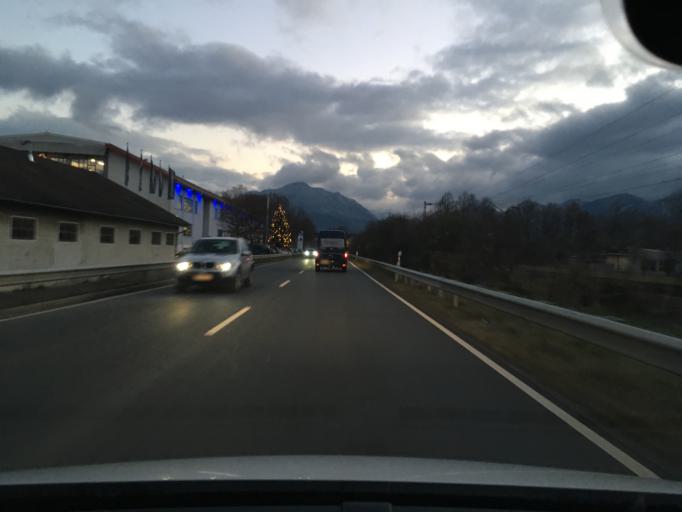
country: DE
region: Bavaria
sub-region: Upper Bavaria
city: Raubling
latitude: 47.7759
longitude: 12.1049
